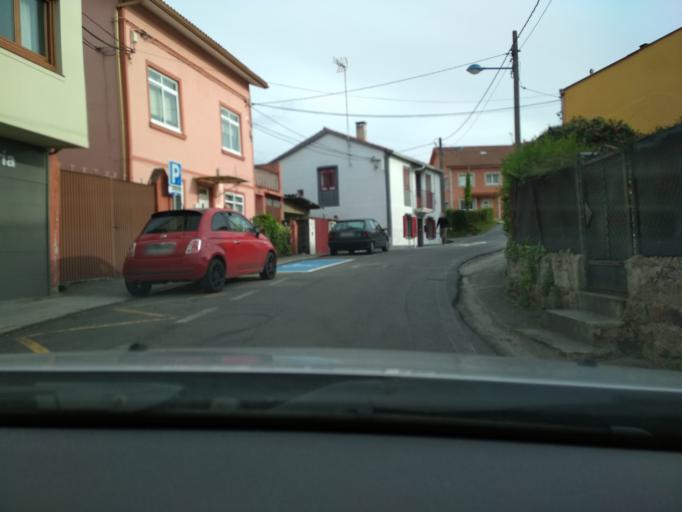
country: ES
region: Galicia
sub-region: Provincia da Coruna
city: Culleredo
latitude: 43.2880
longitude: -8.3897
